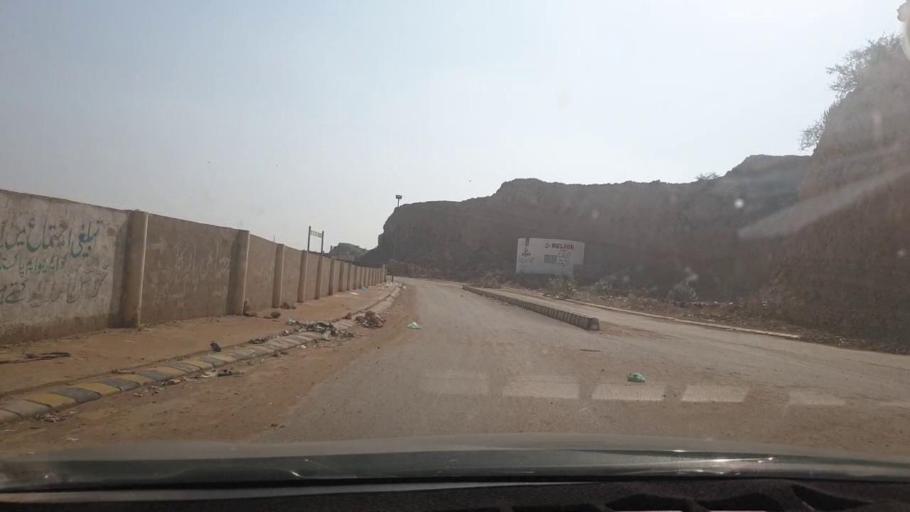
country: PK
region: Sindh
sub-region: Karachi District
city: Karachi
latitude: 24.9683
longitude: 66.9979
